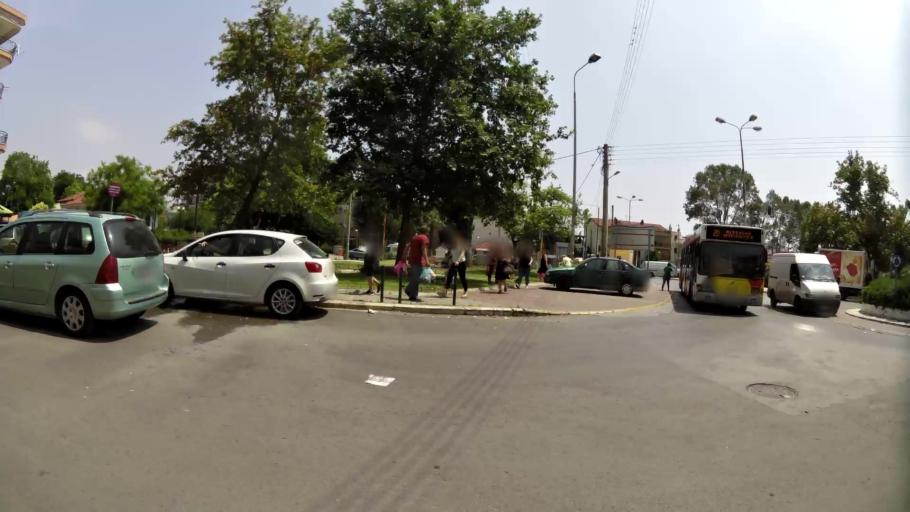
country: GR
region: Central Macedonia
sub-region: Nomos Thessalonikis
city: Evosmos
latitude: 40.6603
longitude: 22.9084
